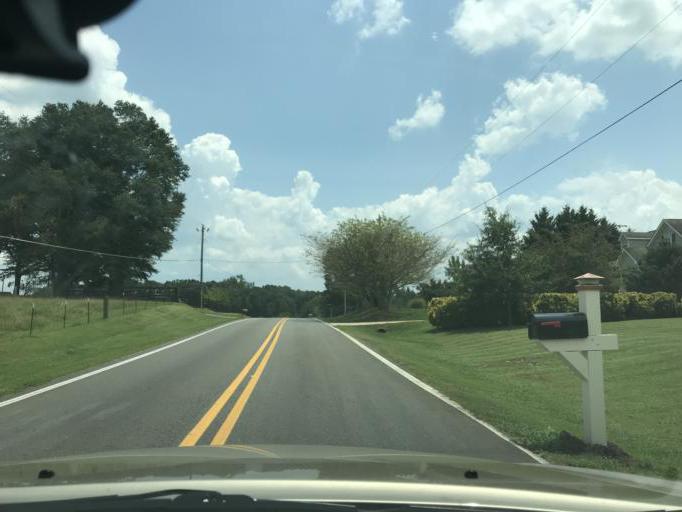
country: US
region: Georgia
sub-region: Forsyth County
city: Cumming
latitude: 34.2686
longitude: -84.2336
